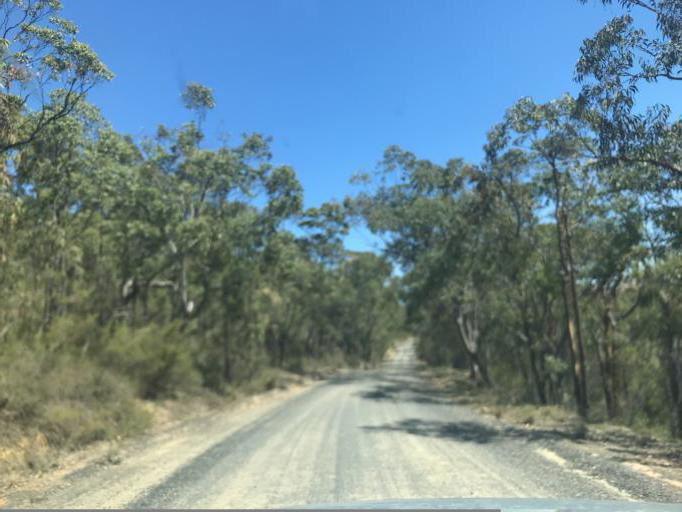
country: AU
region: New South Wales
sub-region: Wyong Shire
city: Little Jilliby
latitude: -33.1481
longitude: 151.0830
